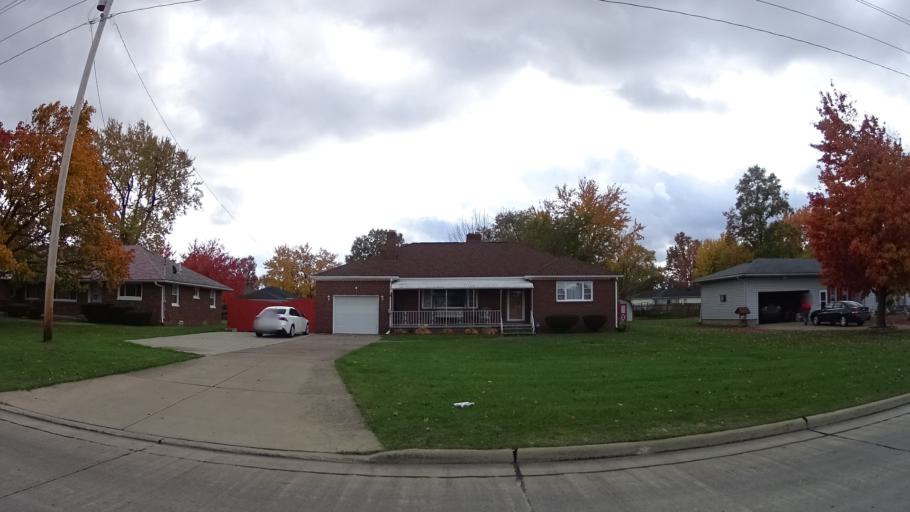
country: US
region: Ohio
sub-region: Lorain County
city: Lorain
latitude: 41.4418
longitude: -82.1902
